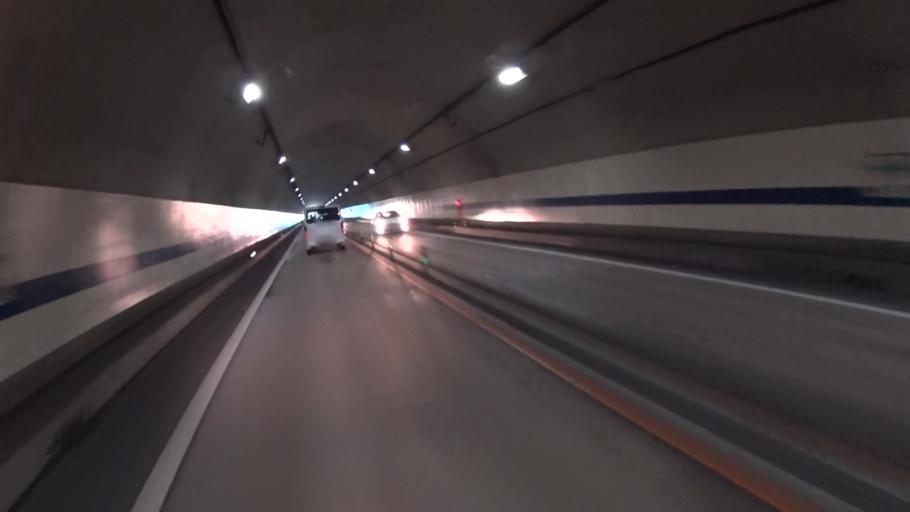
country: JP
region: Kyoto
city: Maizuru
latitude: 35.4129
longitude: 135.2235
